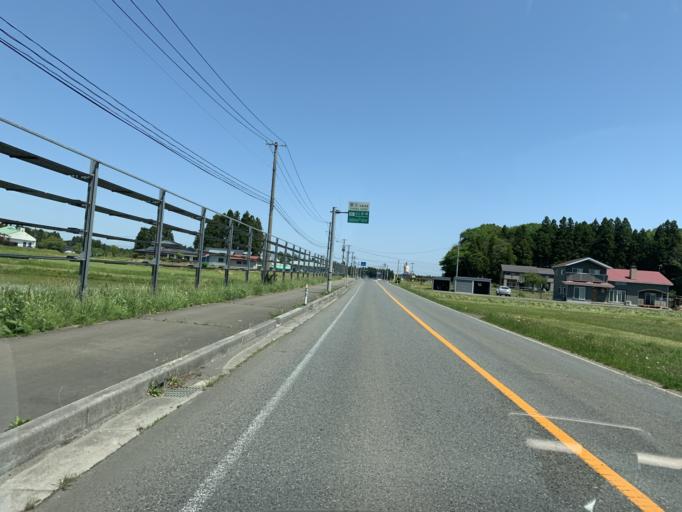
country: JP
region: Iwate
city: Kitakami
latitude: 39.2306
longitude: 141.0665
